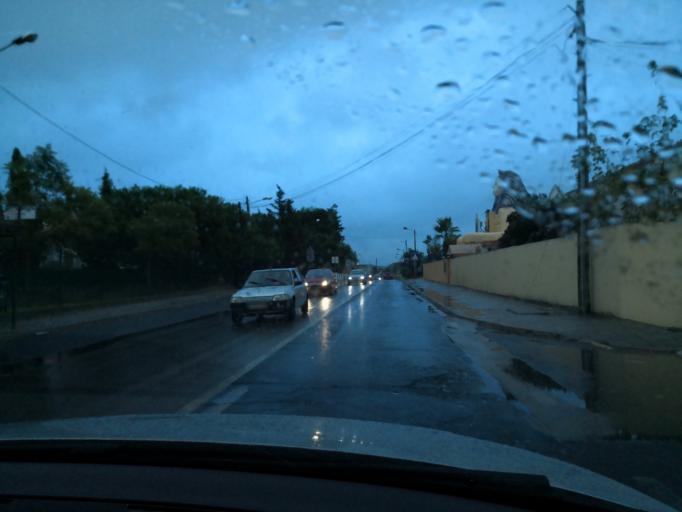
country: PT
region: Setubal
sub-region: Moita
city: Alhos Vedros
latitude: 38.6529
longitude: -9.0205
